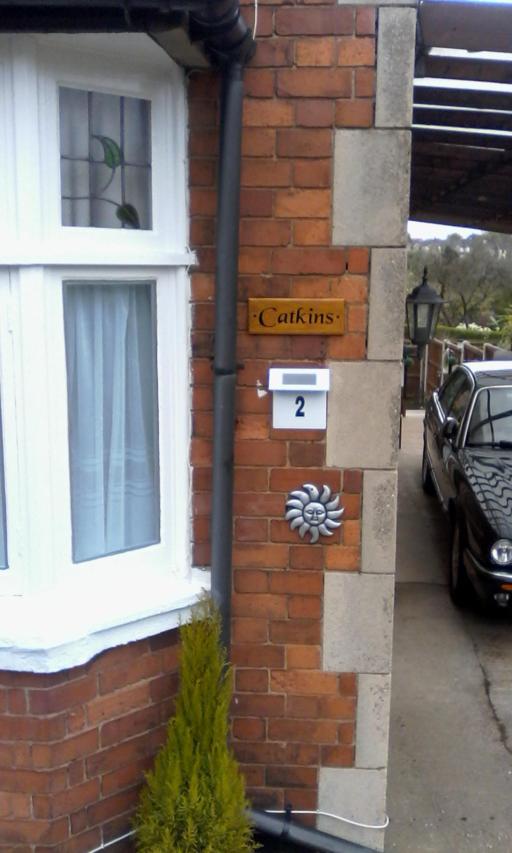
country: GB
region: England
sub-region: Nottingham
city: Nottingham
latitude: 52.9655
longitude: -1.1227
